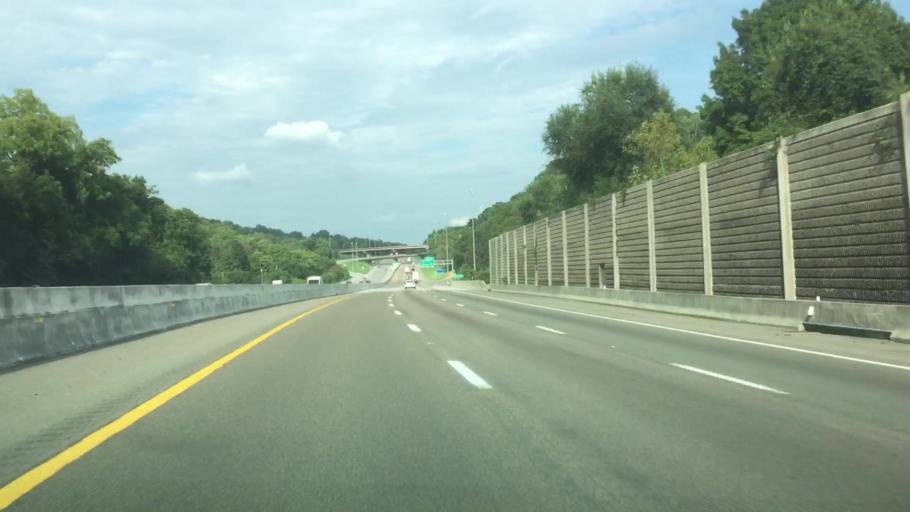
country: US
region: Virginia
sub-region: City of Bristol
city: Bristol
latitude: 36.6211
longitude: -82.1907
